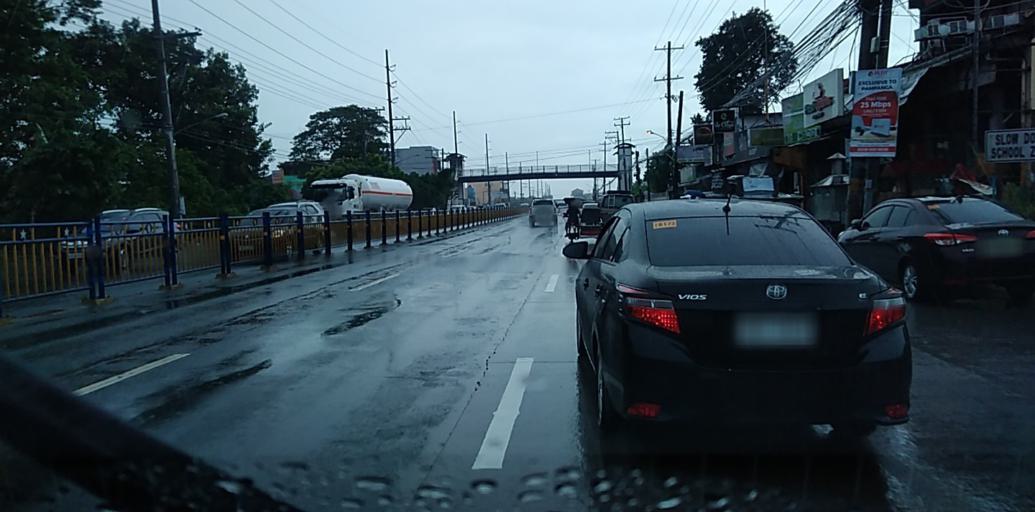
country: PH
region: Central Luzon
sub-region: Province of Pampanga
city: Magliman
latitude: 15.0573
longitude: 120.6584
